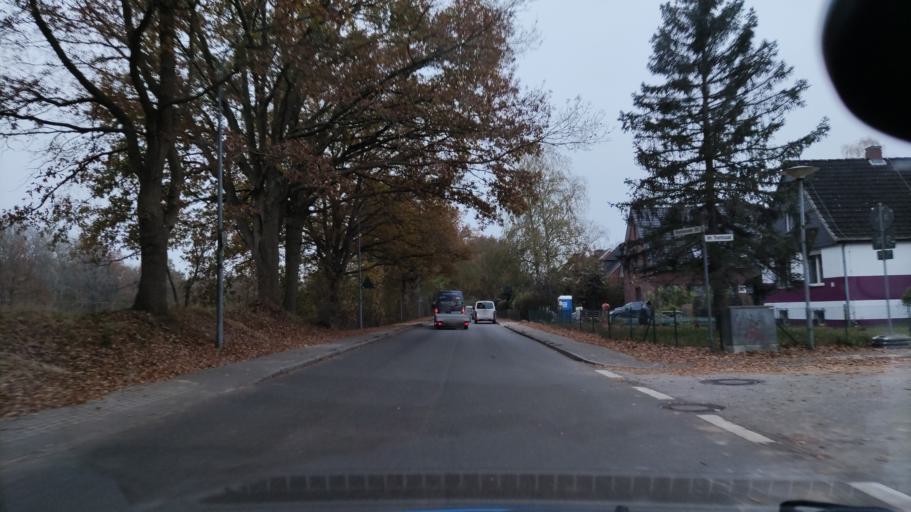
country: DE
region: Schleswig-Holstein
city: Gross Gronau
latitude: 53.8185
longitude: 10.7162
